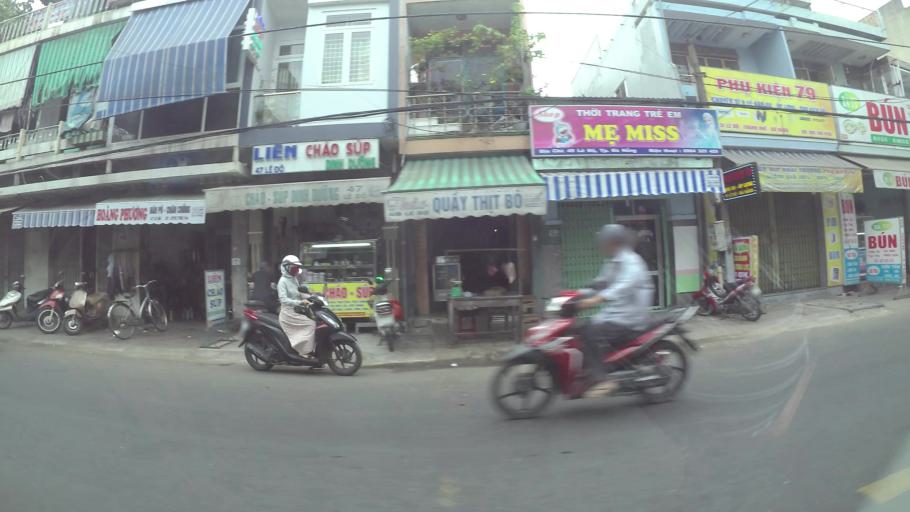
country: VN
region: Da Nang
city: Thanh Khe
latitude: 16.0693
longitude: 108.2015
